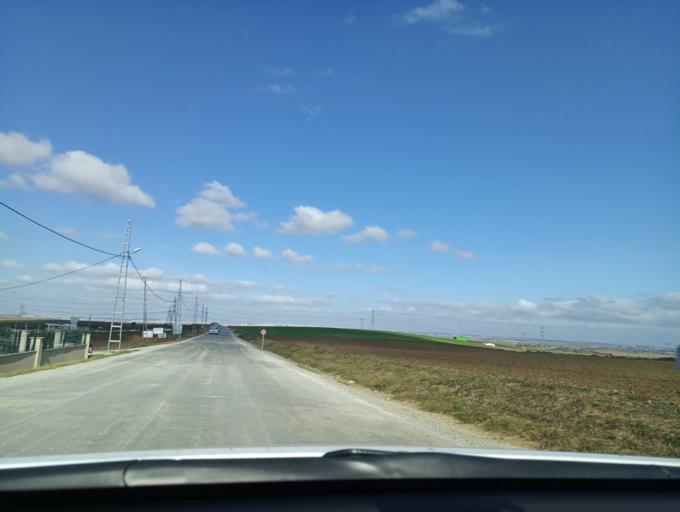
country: TR
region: Tekirdag
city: Corlu
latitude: 41.0516
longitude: 27.8355
